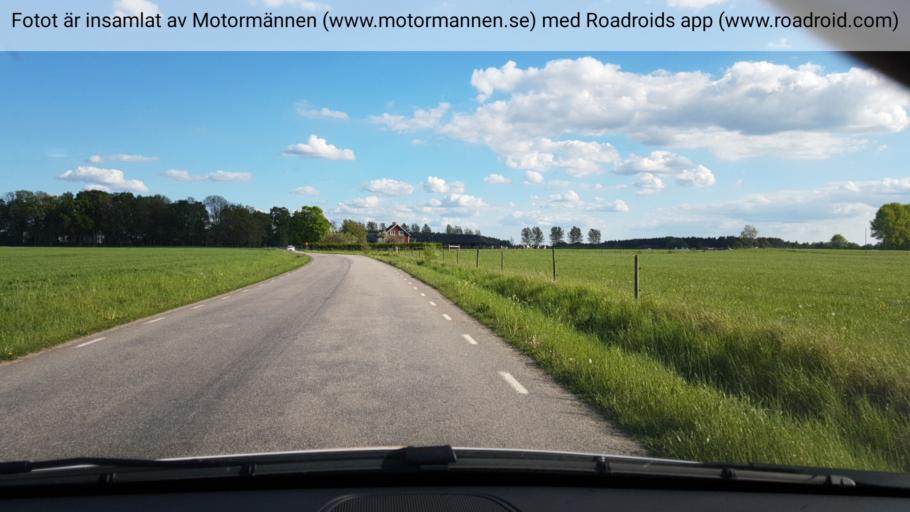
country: SE
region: Vaestra Goetaland
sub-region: Gotene Kommun
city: Kallby
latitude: 58.4676
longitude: 13.3305
